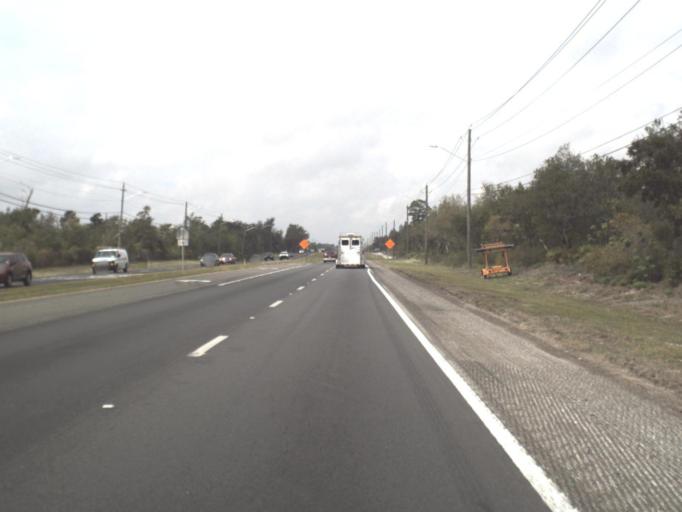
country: US
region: Florida
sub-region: Santa Rosa County
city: Navarre
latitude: 30.4019
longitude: -86.8899
